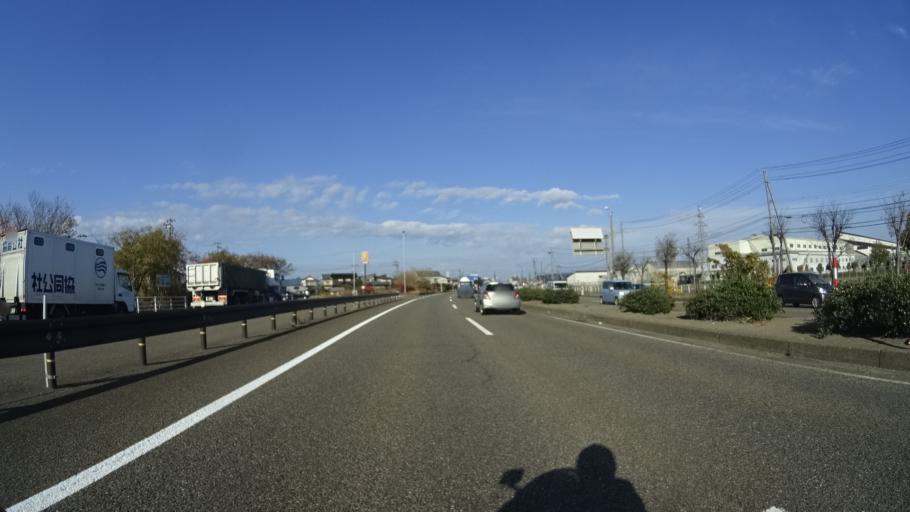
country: JP
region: Niigata
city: Joetsu
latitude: 37.1751
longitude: 138.2665
